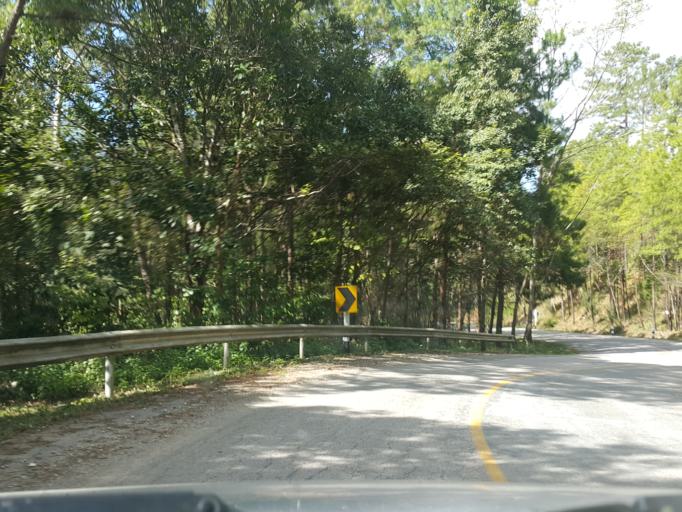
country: TH
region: Mae Hong Son
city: Mae Hi
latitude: 19.2704
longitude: 98.6247
